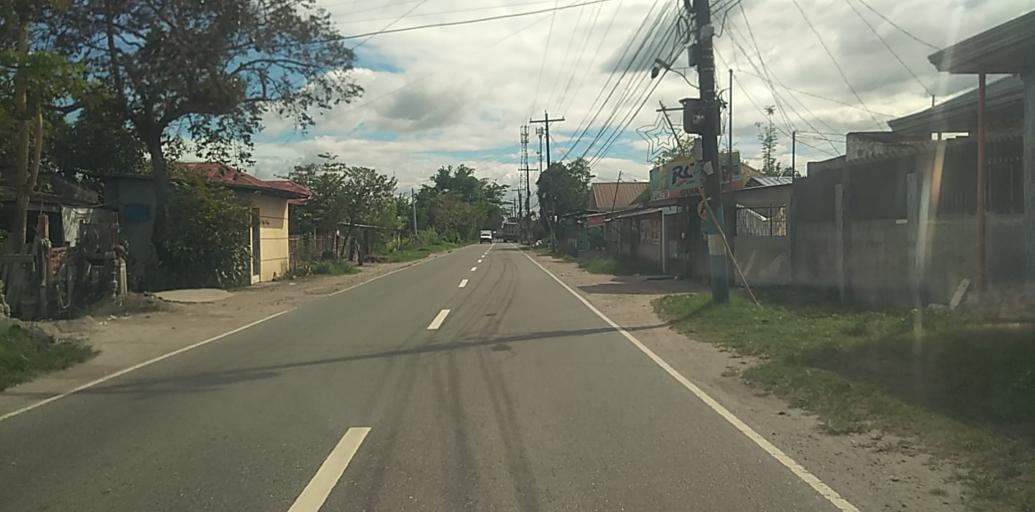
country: PH
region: Central Luzon
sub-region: Province of Pampanga
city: Buensuseso
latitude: 15.1817
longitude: 120.6770
